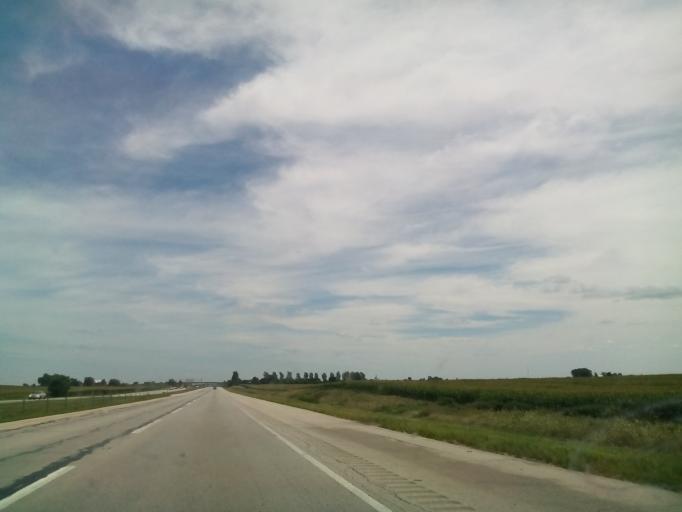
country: US
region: Illinois
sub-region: DeKalb County
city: Malta
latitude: 41.8997
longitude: -88.8600
